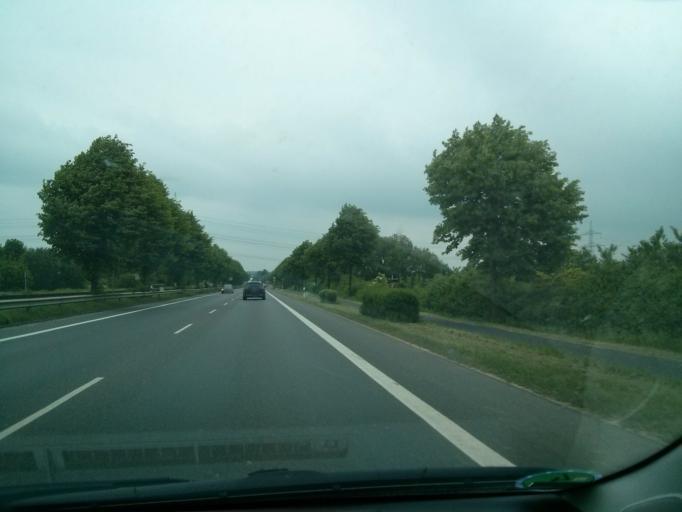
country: DE
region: North Rhine-Westphalia
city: Meckenheim
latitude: 50.6274
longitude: 7.0028
